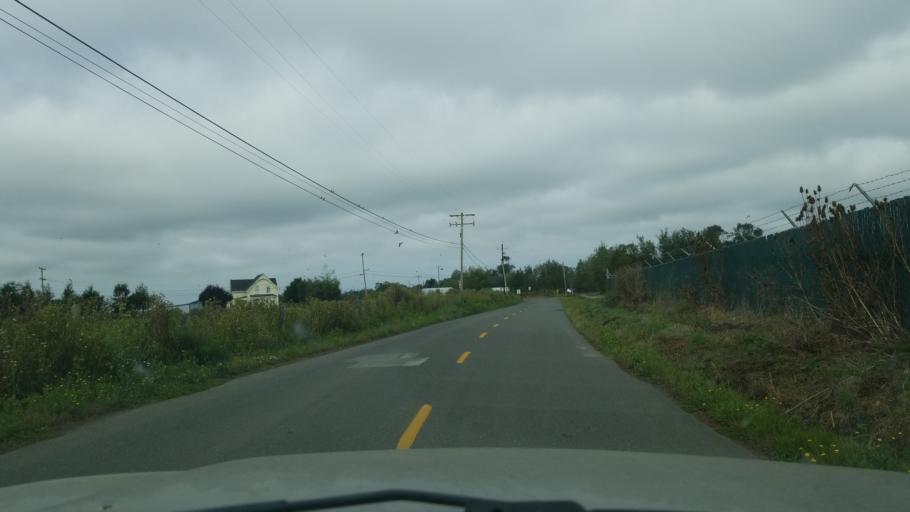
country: US
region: California
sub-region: Humboldt County
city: Ferndale
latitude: 40.5930
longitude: -124.2606
